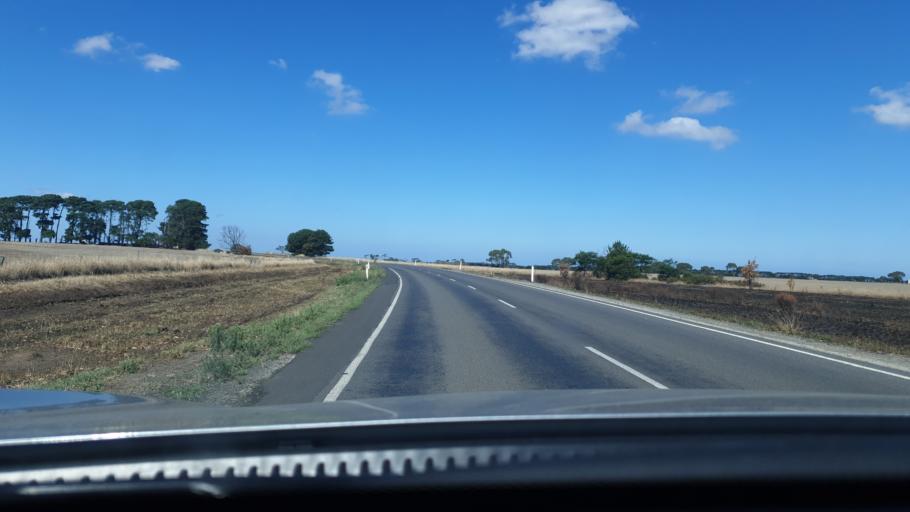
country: AU
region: Victoria
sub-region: Warrnambool
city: Warrnambool
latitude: -38.1682
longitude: 142.3989
